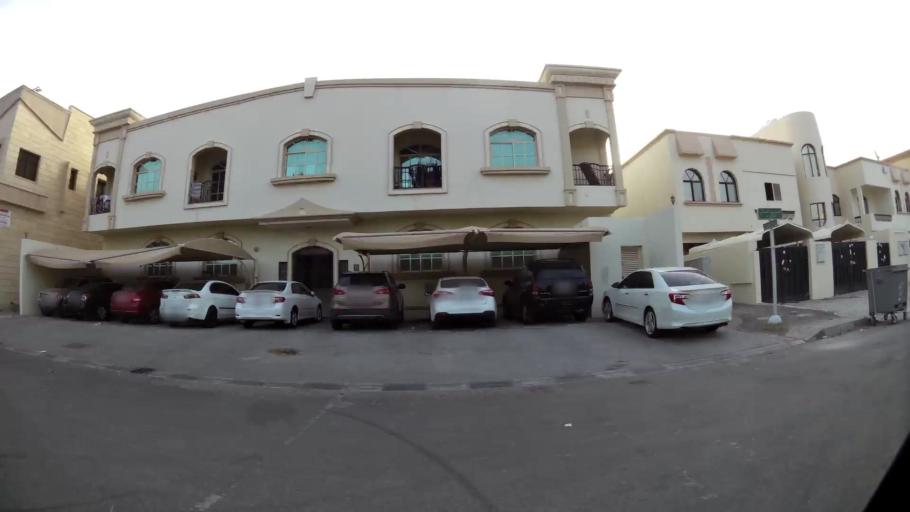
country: AE
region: Abu Dhabi
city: Al Ain
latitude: 24.2429
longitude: 55.7287
